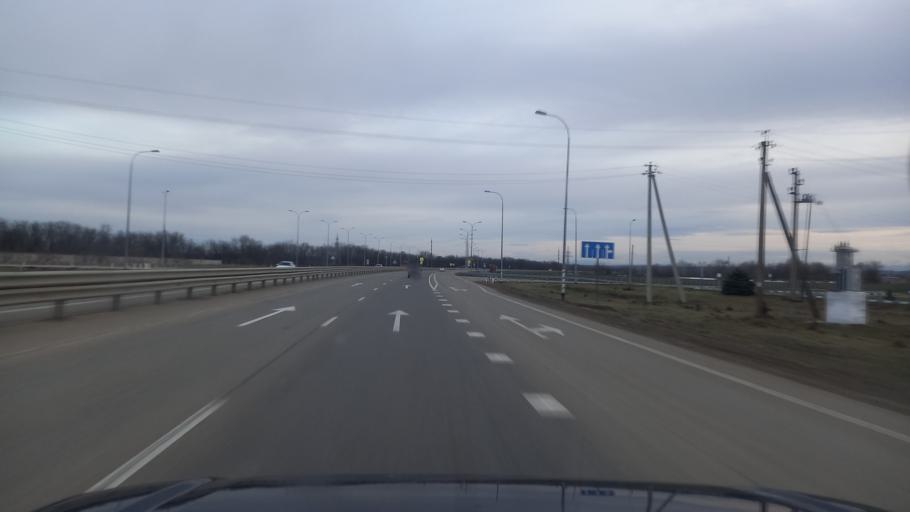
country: RU
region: Adygeya
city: Khanskaya
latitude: 44.6808
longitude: 39.9879
